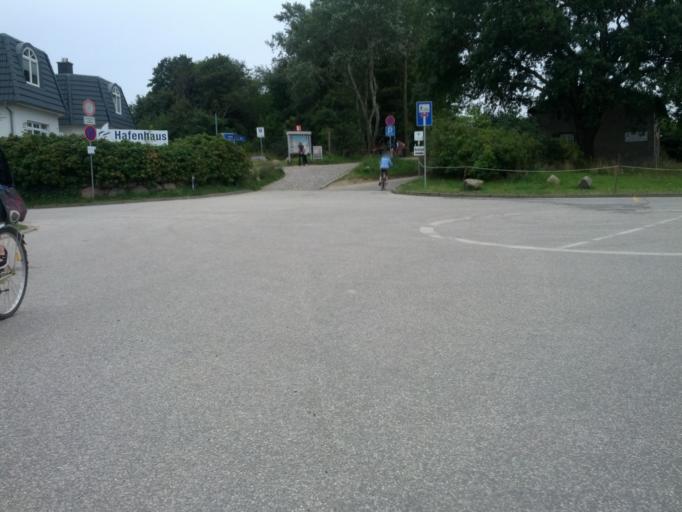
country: DE
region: Mecklenburg-Vorpommern
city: Ostseebad Kuhlungsborn
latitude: 54.1508
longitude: 11.7714
